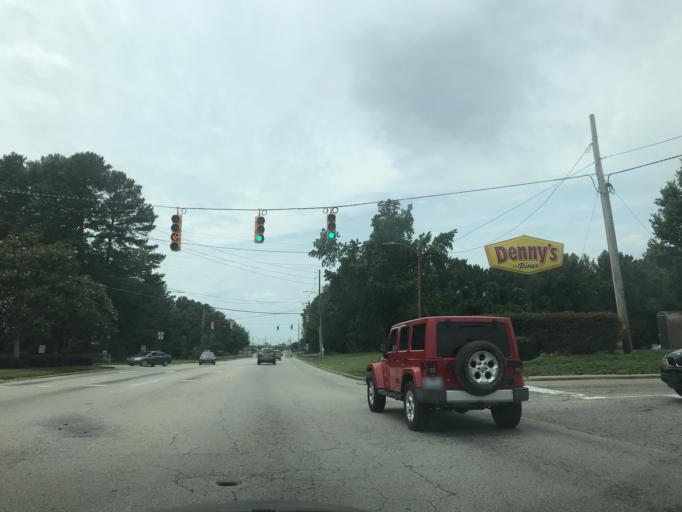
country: US
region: North Carolina
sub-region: Vance County
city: Henderson
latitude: 36.3330
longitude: -78.4356
